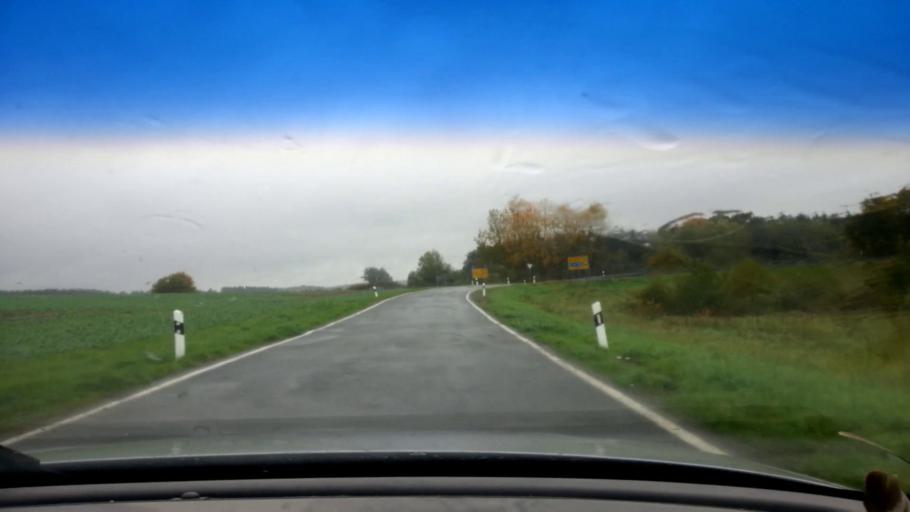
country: DE
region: Bavaria
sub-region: Upper Franconia
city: Stadelhofen
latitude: 50.0065
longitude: 11.1991
